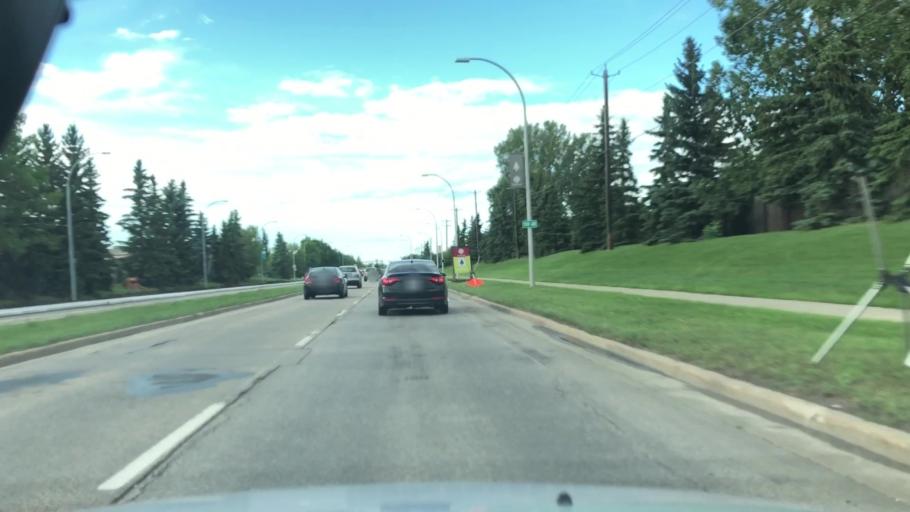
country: CA
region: Alberta
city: St. Albert
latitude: 53.6183
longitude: -113.5411
